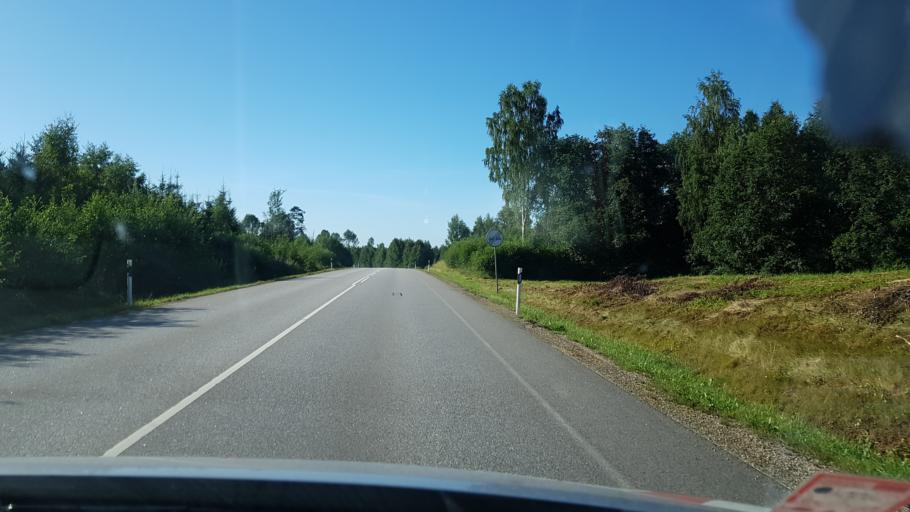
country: EE
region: Valgamaa
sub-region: Valga linn
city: Valga
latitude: 57.7405
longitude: 26.1437
